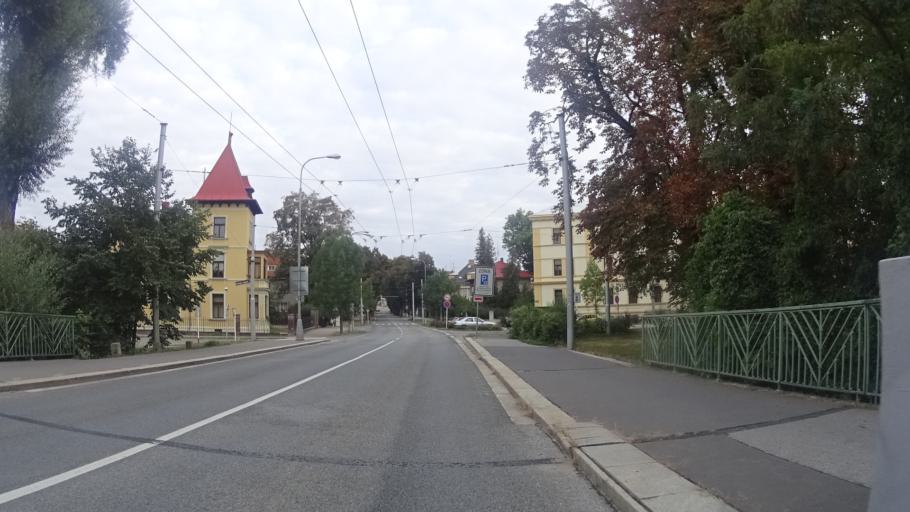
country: CZ
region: Kralovehradecky
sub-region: Okres Hradec Kralove
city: Hradec Kralove
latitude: 50.2077
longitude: 15.8416
